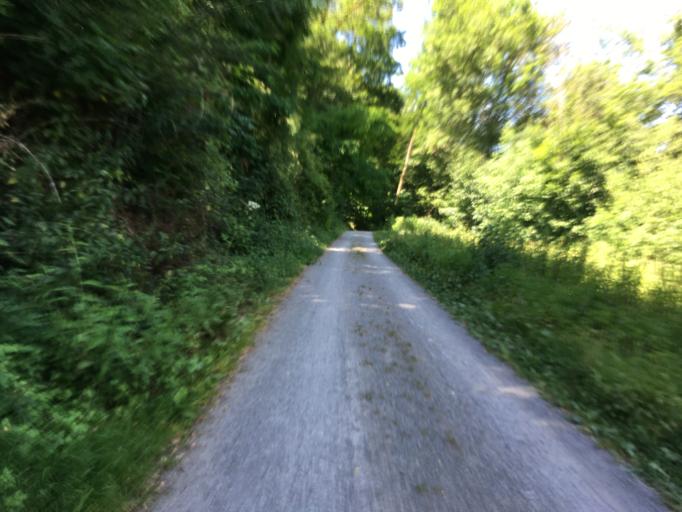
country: DE
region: Baden-Wuerttemberg
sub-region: Regierungsbezirk Stuttgart
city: Vaihingen an der Enz
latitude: 48.9177
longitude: 8.9540
